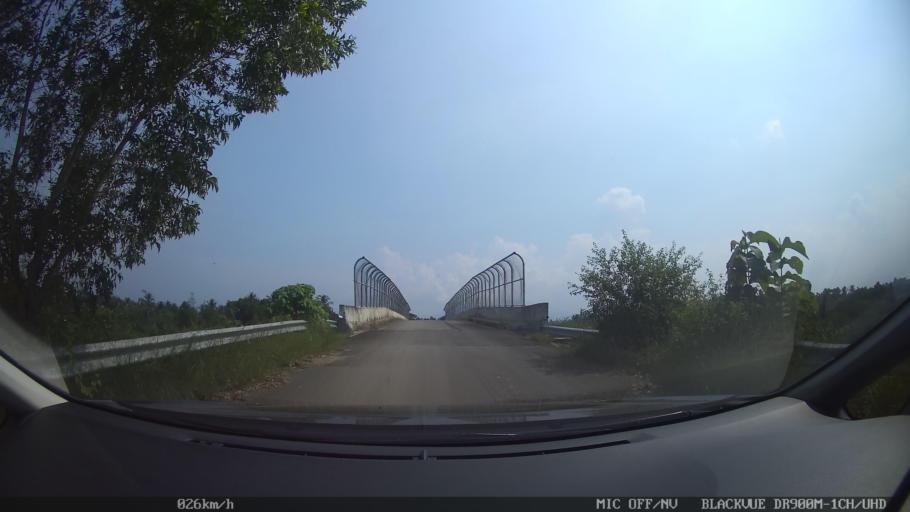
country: ID
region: Lampung
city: Natar
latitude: -5.2936
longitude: 105.2368
